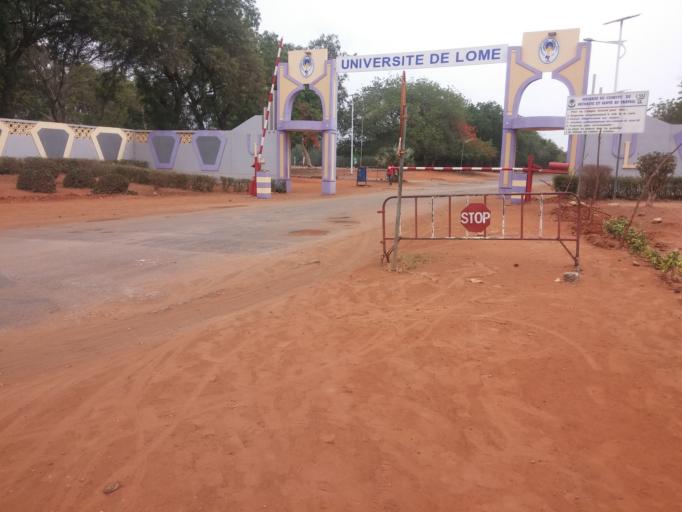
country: TG
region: Maritime
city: Lome
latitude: 6.1717
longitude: 1.2195
